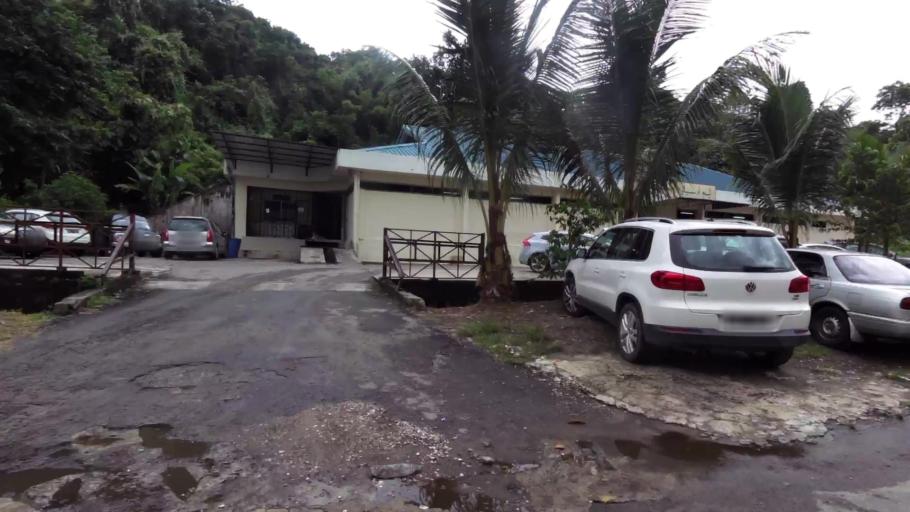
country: BN
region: Brunei and Muara
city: Bandar Seri Begawan
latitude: 4.8970
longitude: 114.9437
